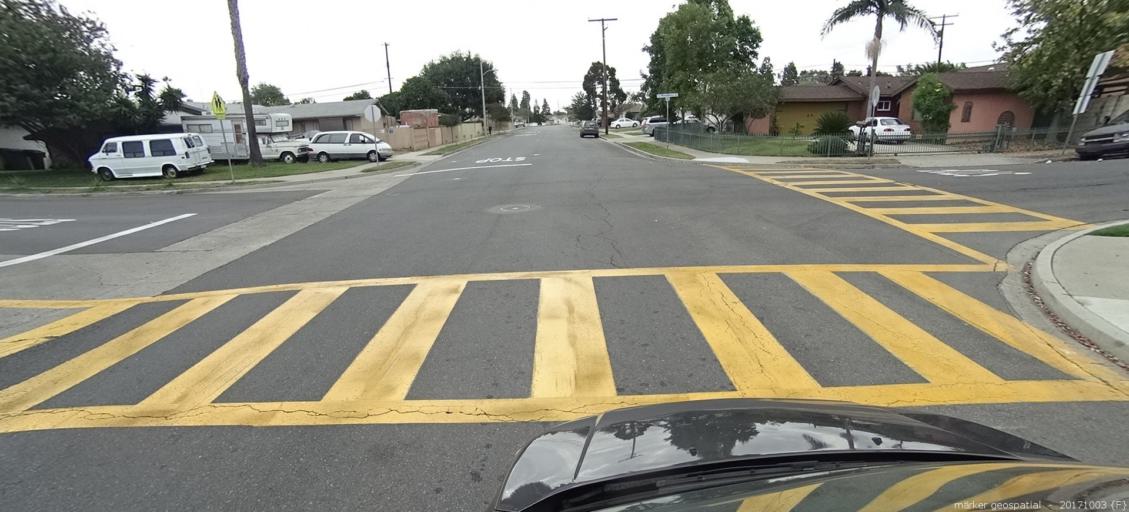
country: US
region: California
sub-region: Orange County
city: Garden Grove
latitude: 33.7631
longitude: -117.9495
